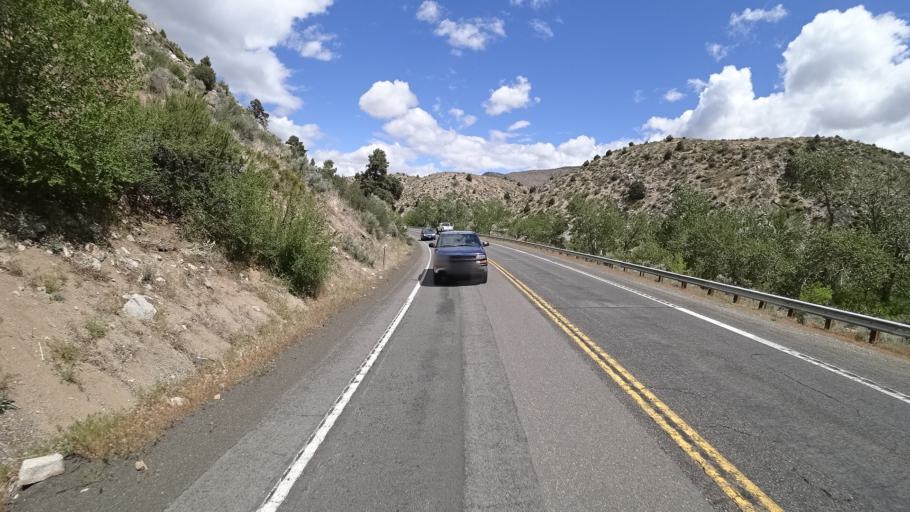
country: US
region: Nevada
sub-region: Lyon County
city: Smith Valley
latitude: 38.5110
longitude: -119.4502
